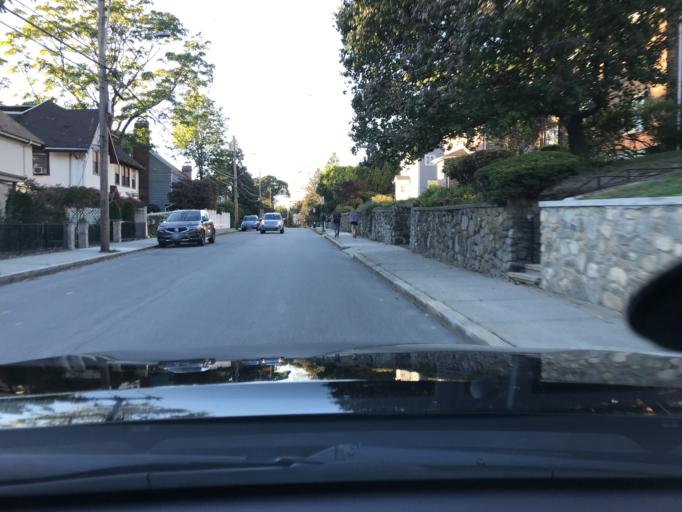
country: US
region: Massachusetts
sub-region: Norfolk County
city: Brookline
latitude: 42.3343
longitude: -71.1354
